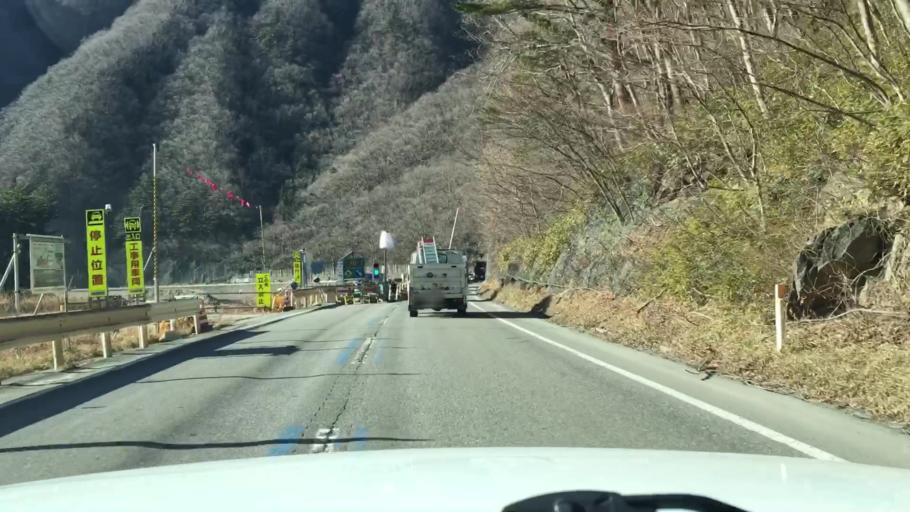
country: JP
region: Iwate
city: Miyako
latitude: 39.6274
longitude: 141.8144
